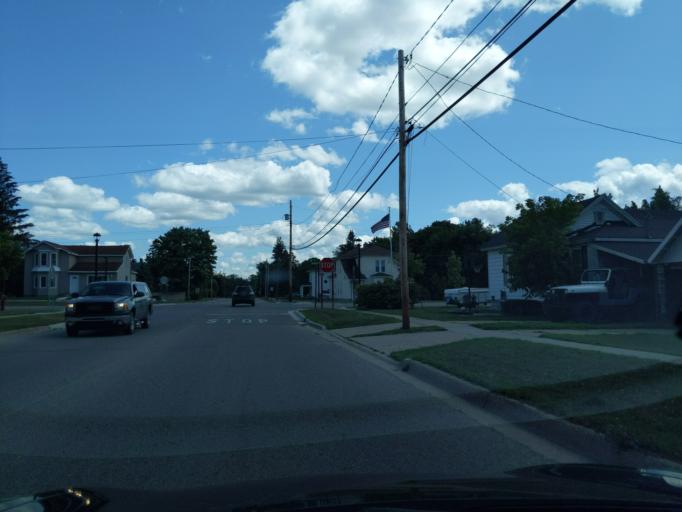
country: US
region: Michigan
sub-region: Crawford County
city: Grayling
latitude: 44.6643
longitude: -84.7118
